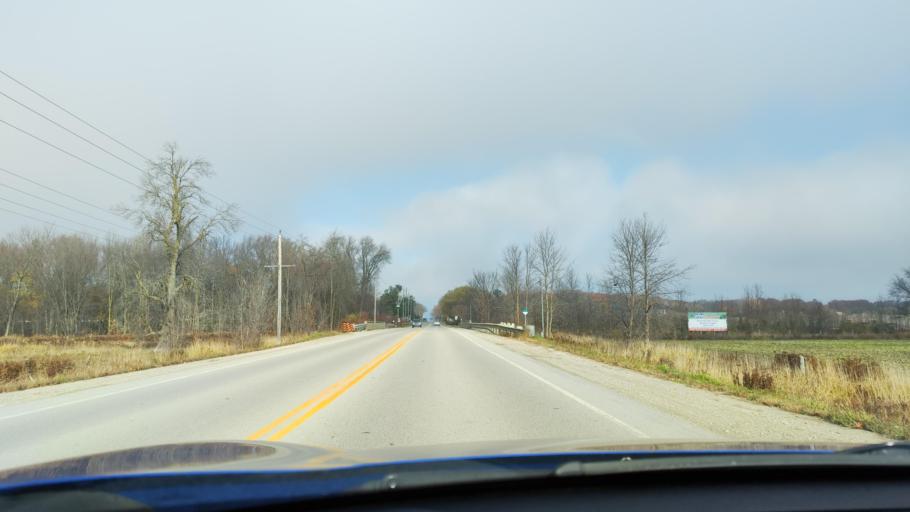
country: CA
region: Ontario
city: Wasaga Beach
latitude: 44.4606
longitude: -80.0728
